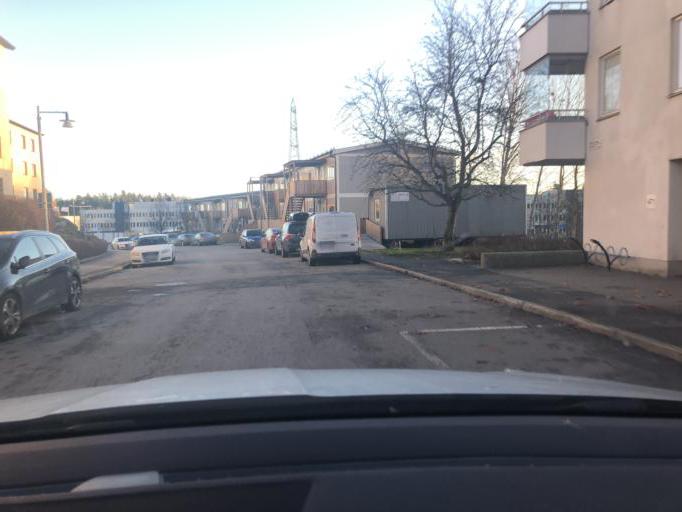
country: SE
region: Stockholm
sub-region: Huddinge Kommun
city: Segeltorp
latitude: 59.2827
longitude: 17.9170
